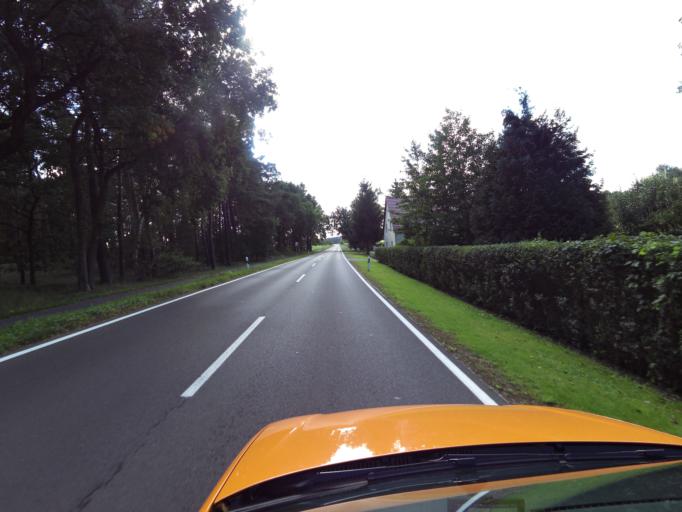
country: DE
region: Brandenburg
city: Michendorf
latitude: 52.2833
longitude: 13.0687
